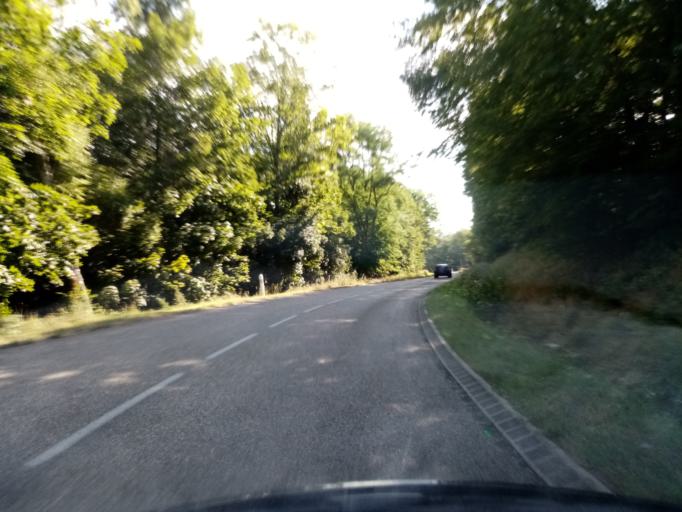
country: FR
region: Alsace
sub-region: Departement du Bas-Rhin
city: Ville
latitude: 48.3417
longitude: 7.3663
